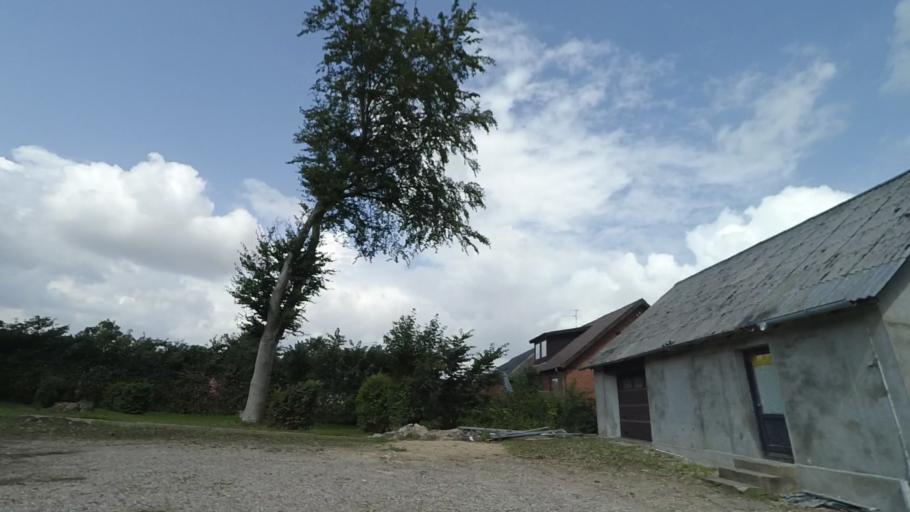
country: DK
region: Central Jutland
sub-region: Norddjurs Kommune
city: Allingabro
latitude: 56.5005
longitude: 10.3393
